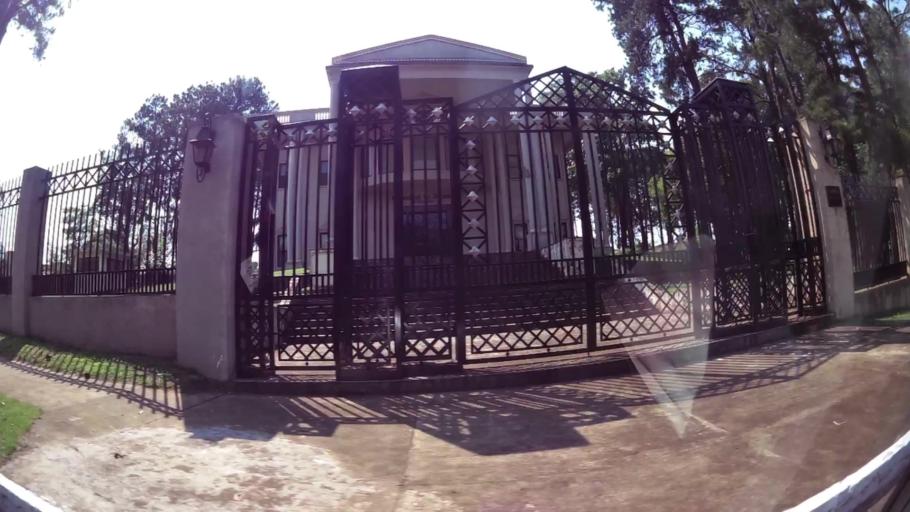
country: PY
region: Alto Parana
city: Ciudad del Este
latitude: -25.5185
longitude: -54.6172
